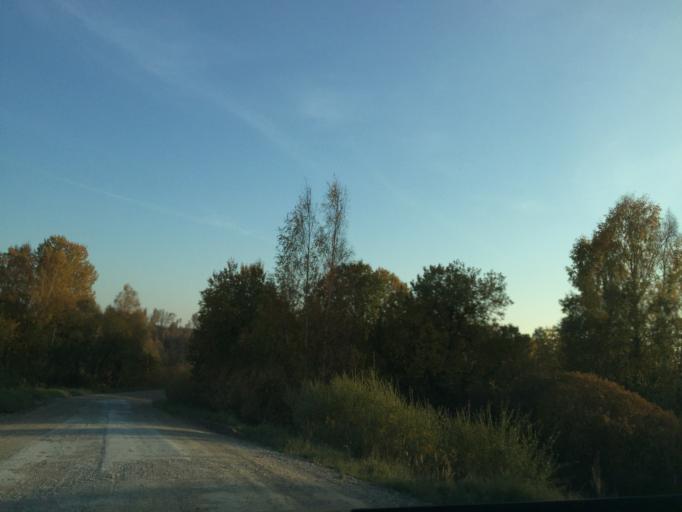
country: LV
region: Vainode
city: Vainode
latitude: 56.5282
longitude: 21.8274
